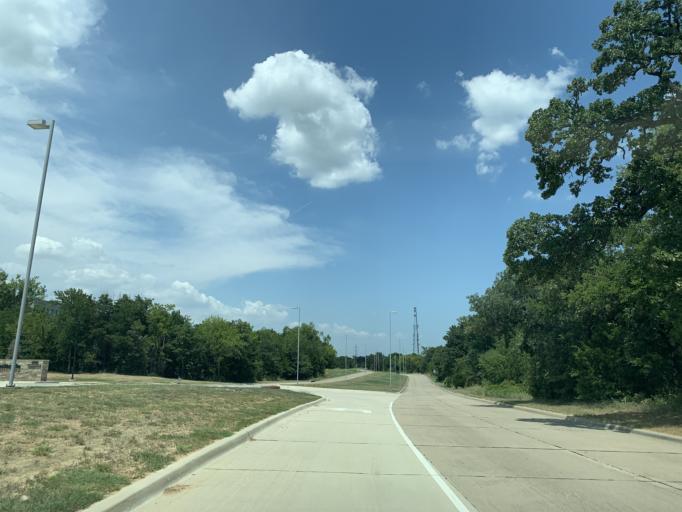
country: US
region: Texas
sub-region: Denton County
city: Trophy Club
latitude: 32.9788
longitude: -97.1586
